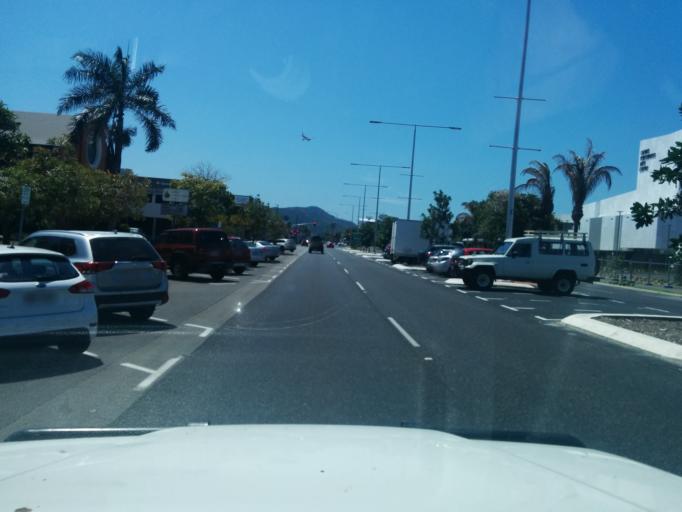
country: AU
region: Queensland
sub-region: Cairns
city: Cairns
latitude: -16.9218
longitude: 145.7720
